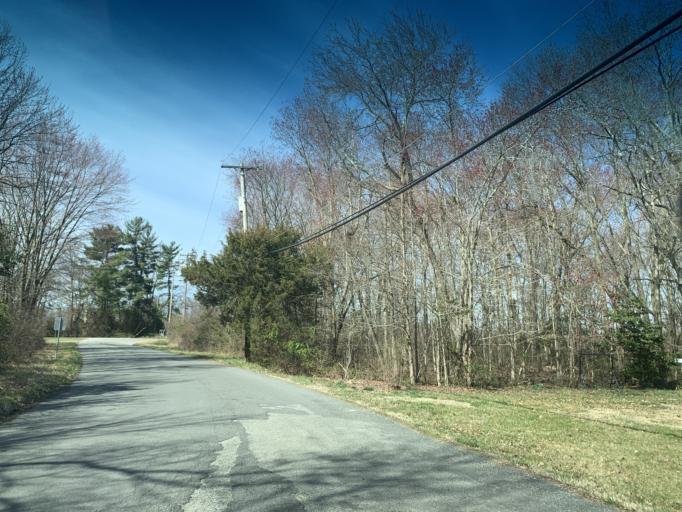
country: US
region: Maryland
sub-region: Cecil County
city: Charlestown
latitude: 39.5474
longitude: -76.0090
